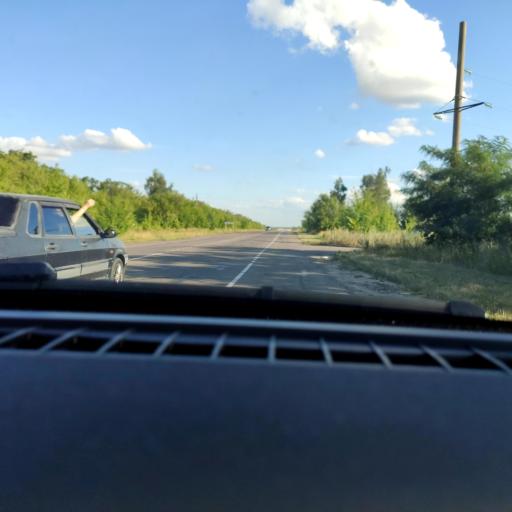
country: RU
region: Voronezj
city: Novaya Usman'
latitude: 51.6180
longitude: 39.3358
